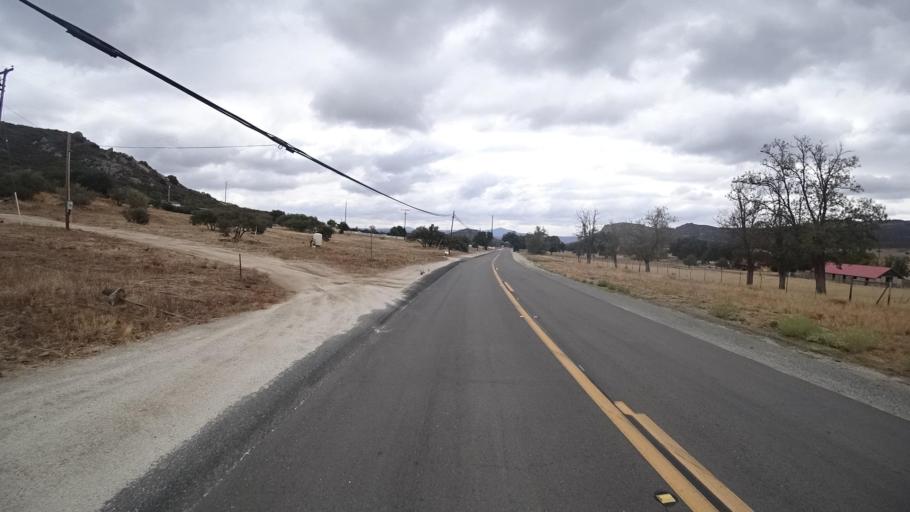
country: US
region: California
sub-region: San Diego County
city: Campo
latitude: 32.6547
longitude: -116.4966
